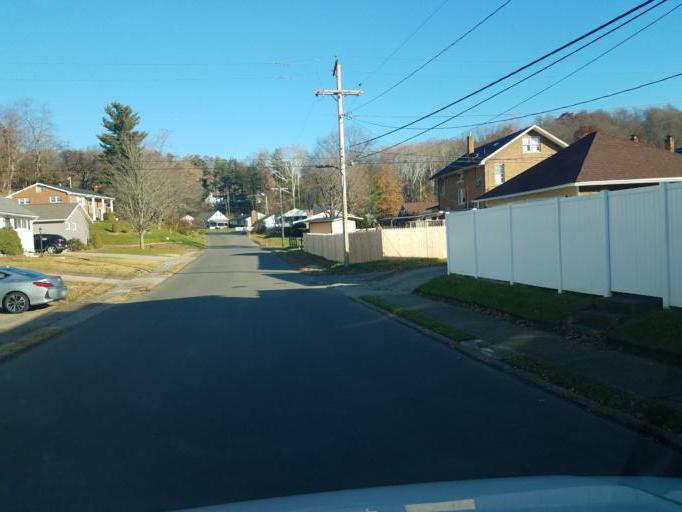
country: US
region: Ohio
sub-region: Scioto County
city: Portsmouth
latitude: 38.7498
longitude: -82.9746
